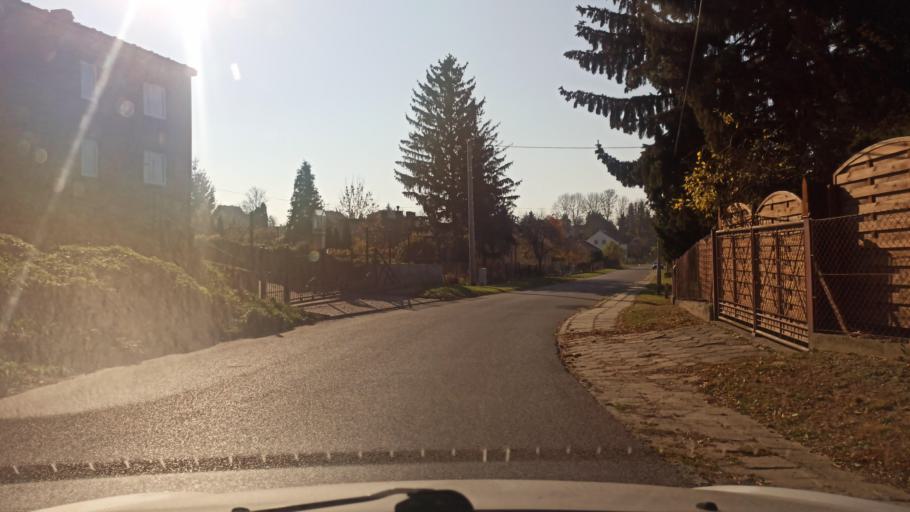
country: PL
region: Subcarpathian Voivodeship
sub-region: Powiat jaroslawski
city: Radymno
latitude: 49.9455
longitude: 22.8222
